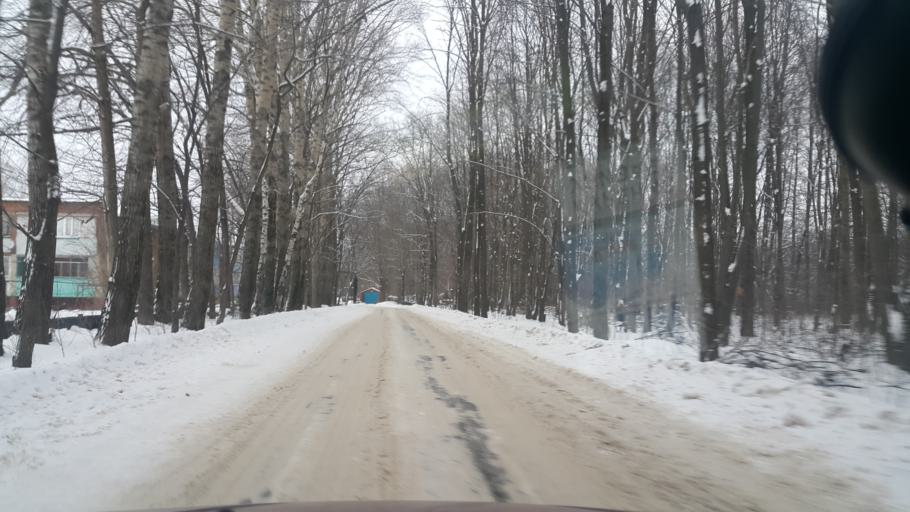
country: RU
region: Tambov
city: Bokino
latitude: 52.6597
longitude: 41.4443
